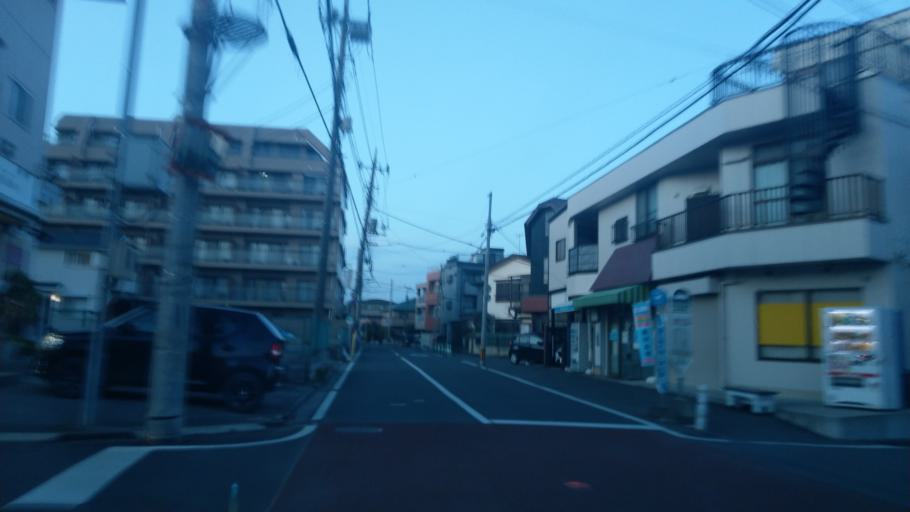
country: JP
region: Saitama
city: Yono
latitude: 35.8776
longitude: 139.6040
